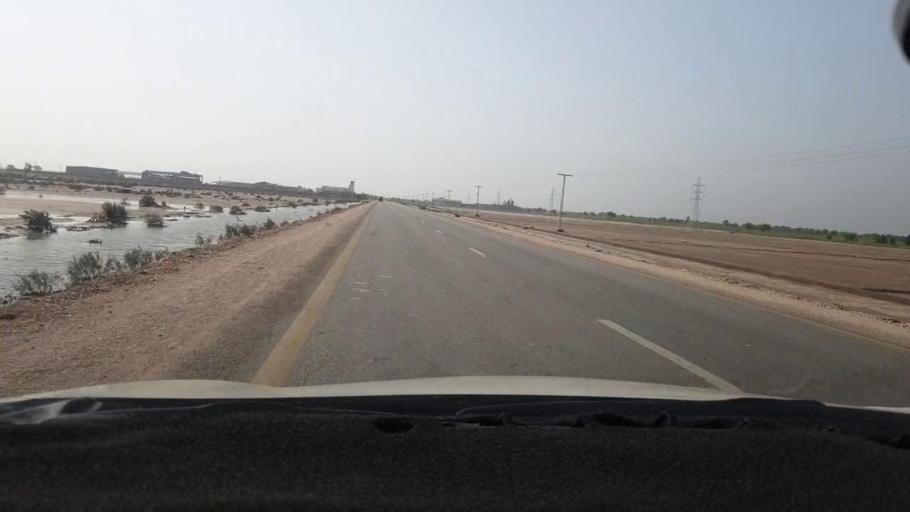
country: PK
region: Sindh
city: Sanghar
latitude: 25.9815
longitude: 68.9682
